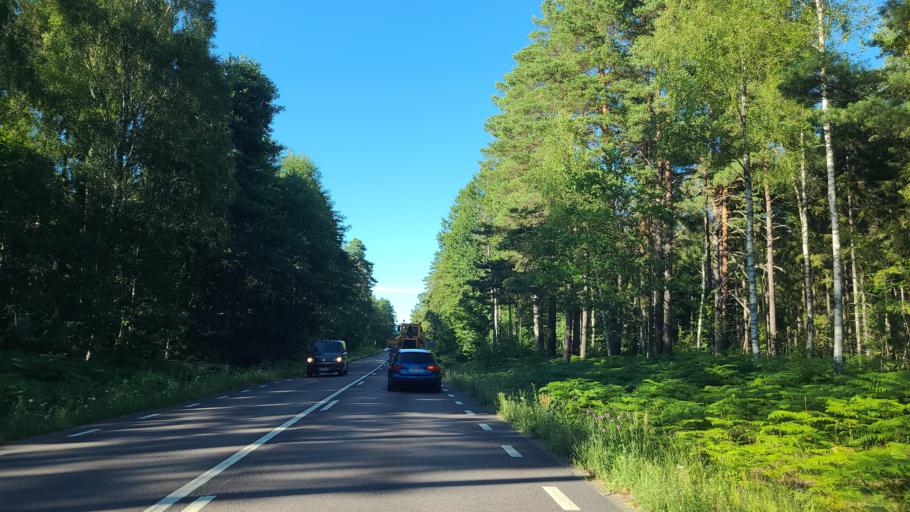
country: SE
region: Kalmar
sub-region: Borgholms Kommun
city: Borgholm
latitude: 57.3018
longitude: 17.0239
